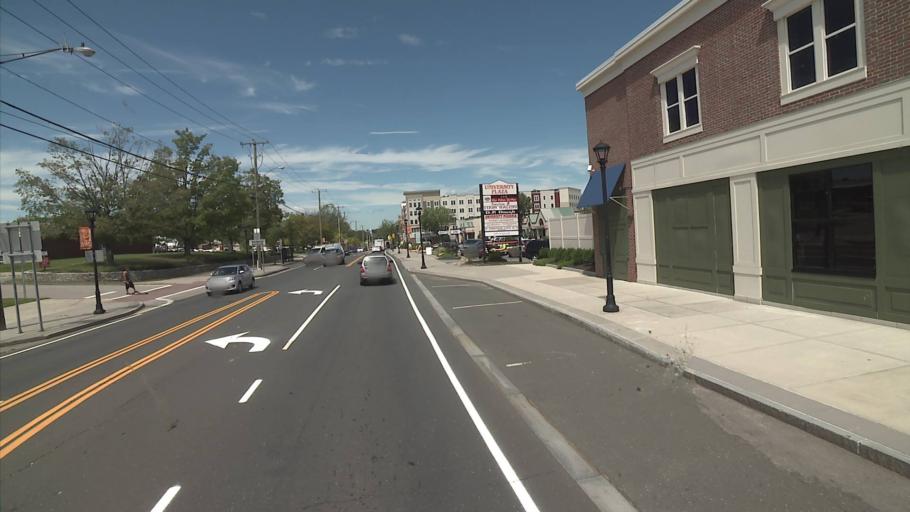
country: US
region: Connecticut
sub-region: Tolland County
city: Storrs
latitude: 41.8023
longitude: -72.2420
